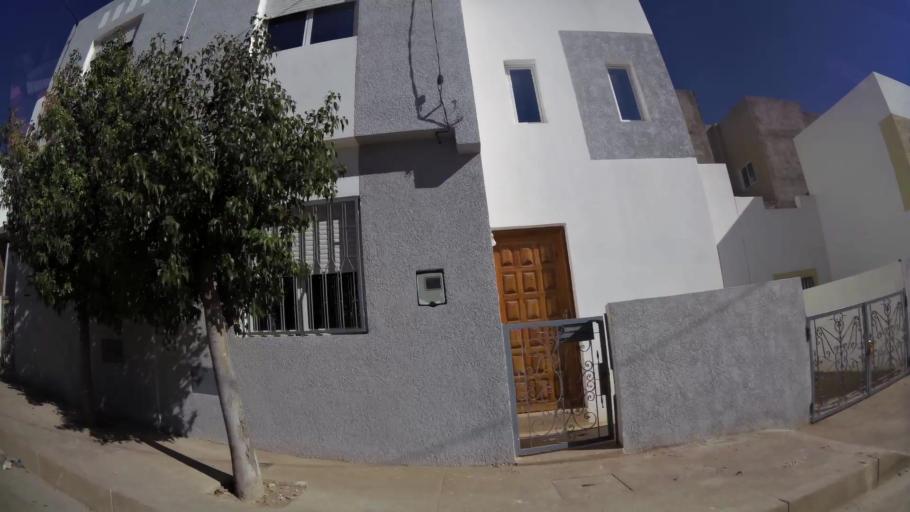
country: MA
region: Oriental
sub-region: Oujda-Angad
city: Oujda
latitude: 34.6473
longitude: -1.8864
